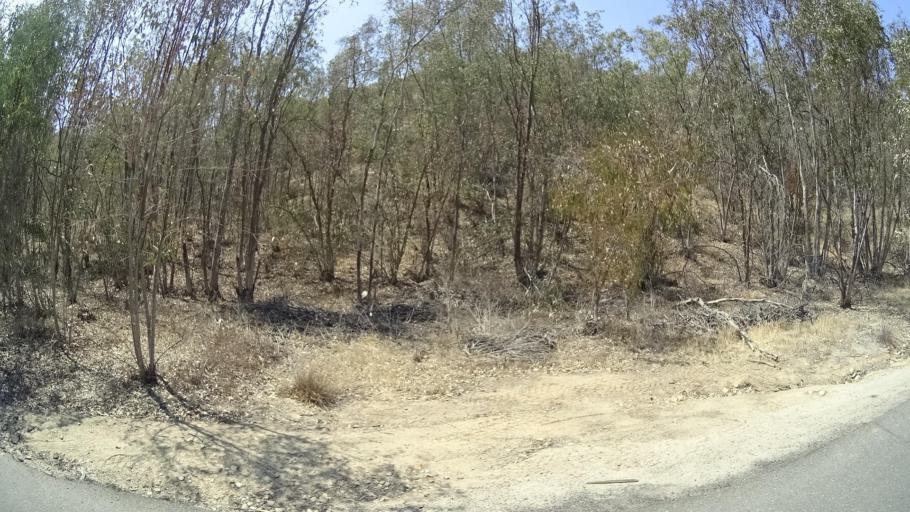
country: US
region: California
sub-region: San Diego County
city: Fallbrook
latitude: 33.4360
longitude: -117.3022
